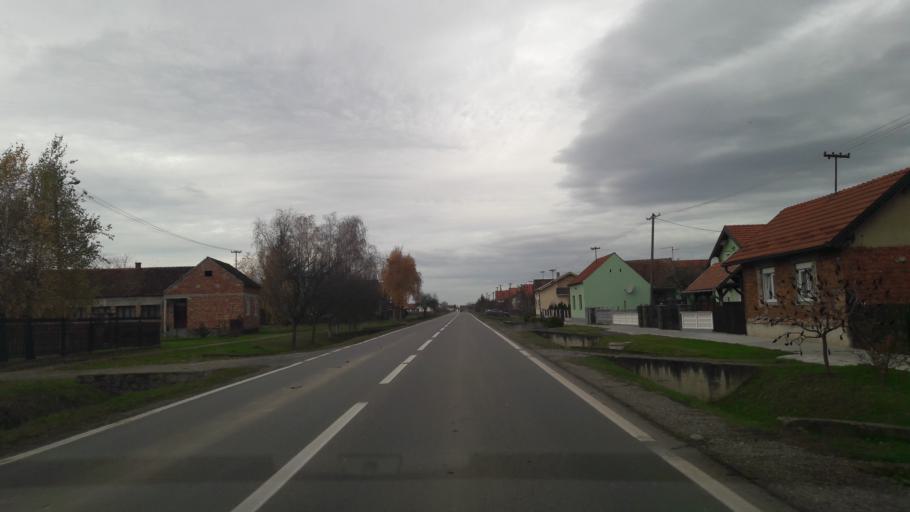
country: HR
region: Osjecko-Baranjska
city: Fericanci
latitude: 45.5286
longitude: 17.9558
